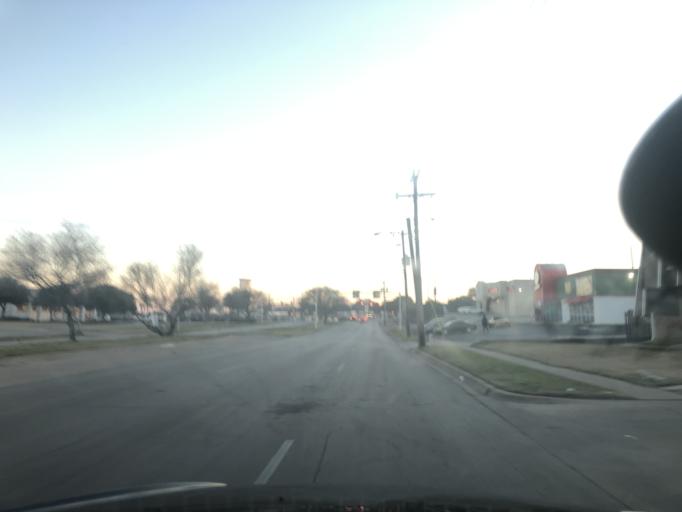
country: US
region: Texas
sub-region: Tarrant County
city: White Settlement
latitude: 32.7262
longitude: -97.4656
